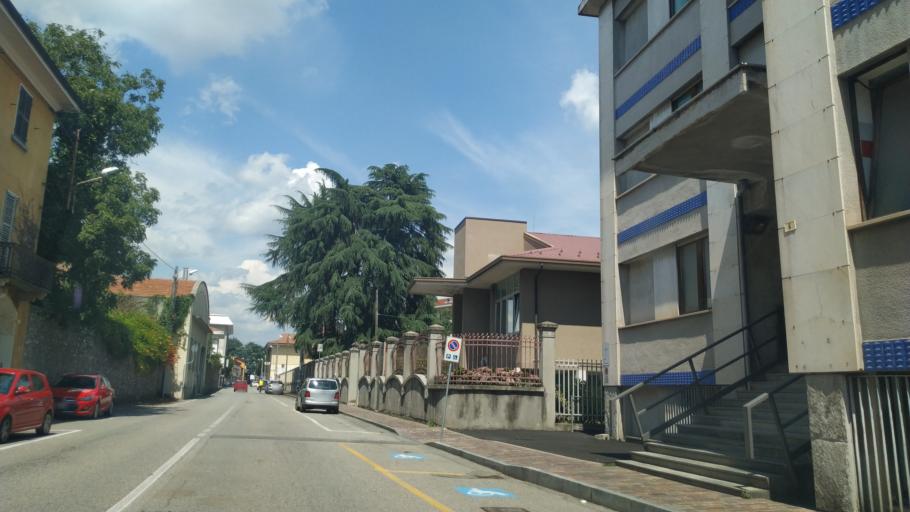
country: IT
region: Piedmont
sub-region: Provincia di Novara
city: Borgomanero
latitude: 45.7034
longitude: 8.4594
